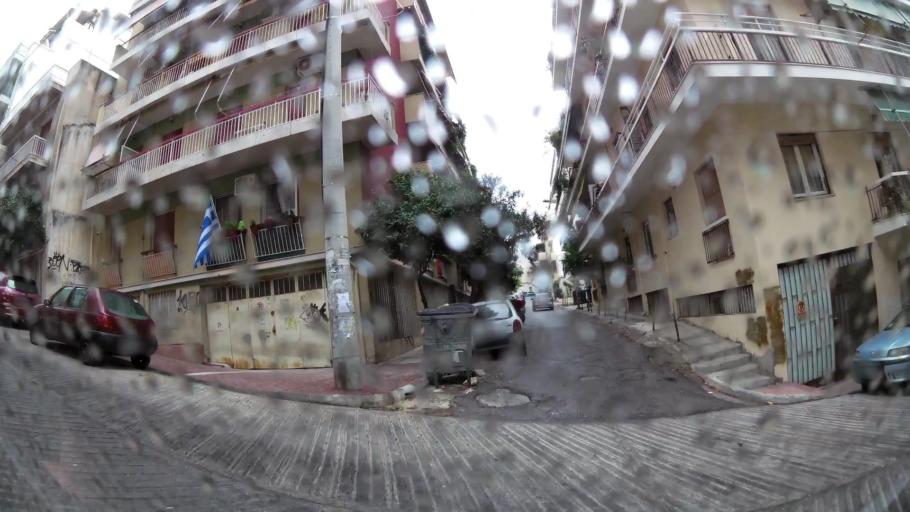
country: GR
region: Attica
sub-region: Nomarchia Athinas
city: Vyronas
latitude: 37.9596
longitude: 23.7479
